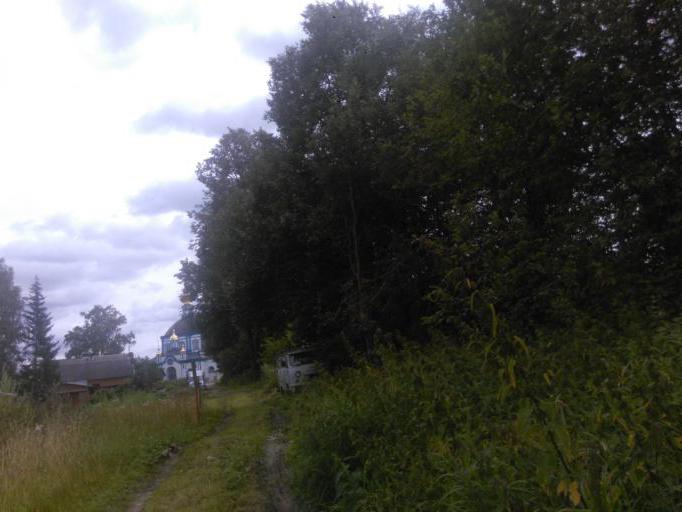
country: RU
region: Moskovskaya
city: Solnechnogorsk
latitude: 56.1489
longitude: 36.9151
